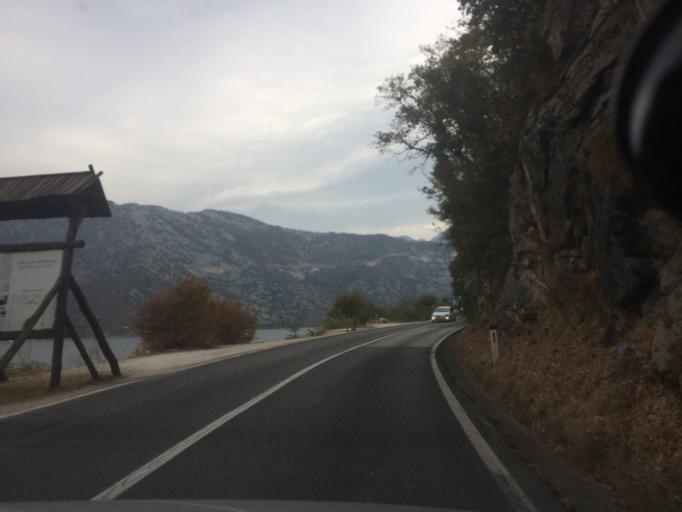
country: ME
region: Kotor
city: Risan
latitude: 42.4920
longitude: 18.6918
